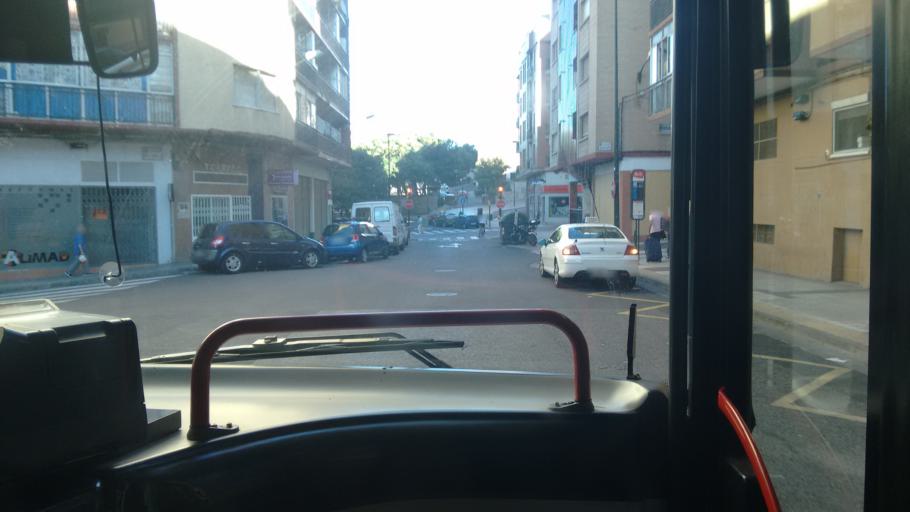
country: ES
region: Aragon
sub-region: Provincia de Zaragoza
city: Zaragoza
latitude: 41.6332
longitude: -0.8771
